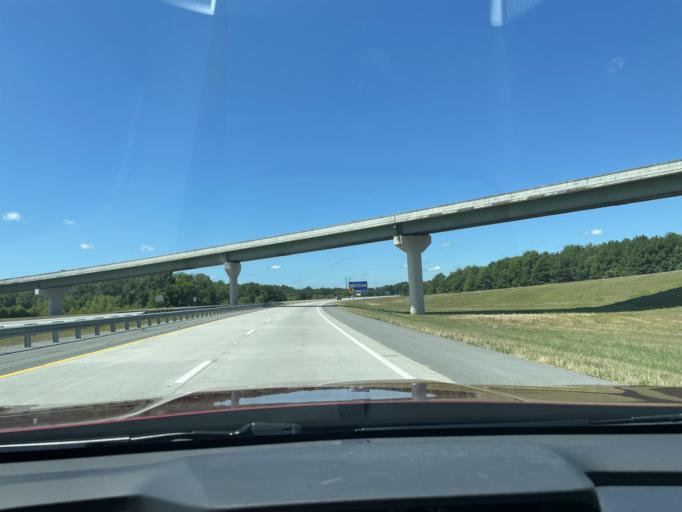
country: US
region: Arkansas
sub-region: Jefferson County
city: Pine Bluff
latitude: 34.1742
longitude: -91.9913
